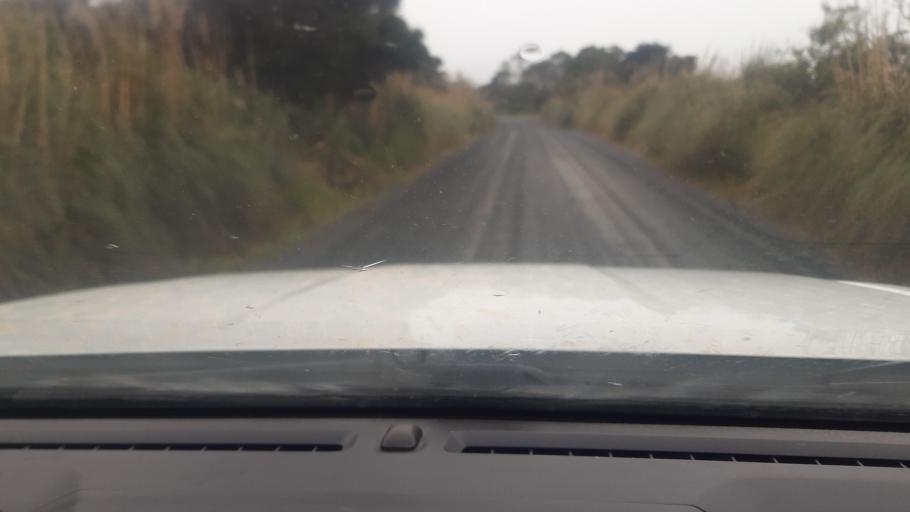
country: NZ
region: Northland
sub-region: Far North District
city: Kaitaia
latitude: -34.9088
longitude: 173.2703
